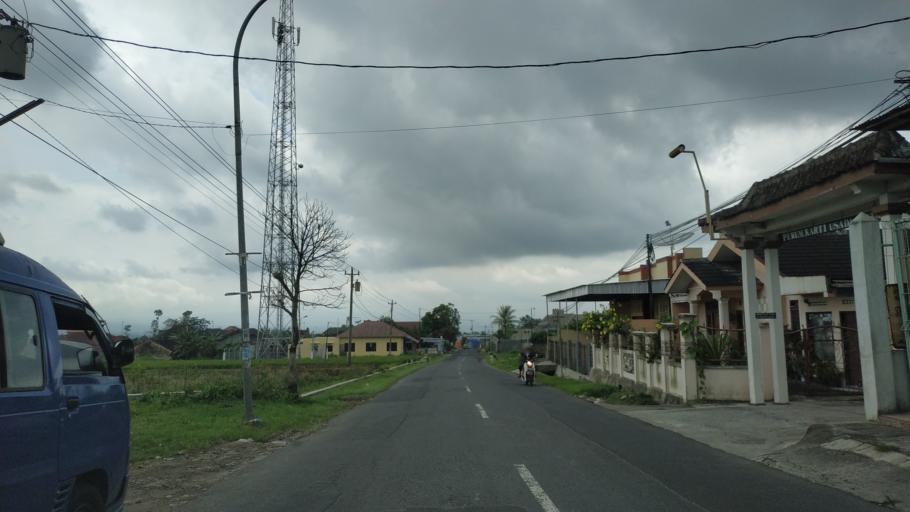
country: ID
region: Central Java
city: Magelang
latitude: -7.2860
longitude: 110.1168
